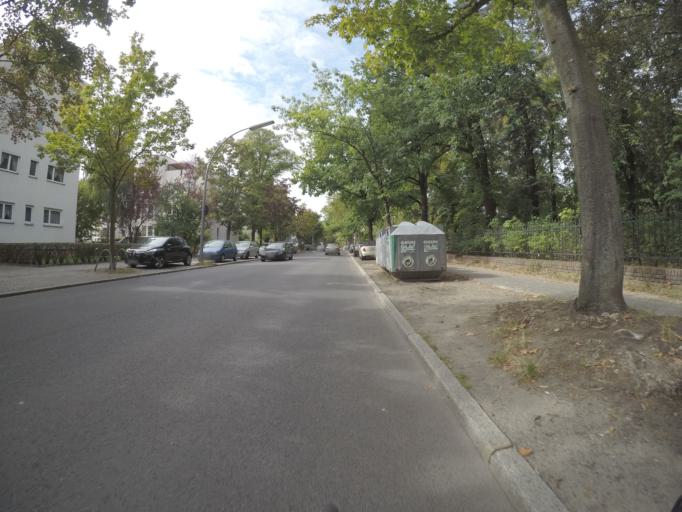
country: DE
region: Berlin
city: Mariendorf
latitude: 52.4475
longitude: 13.3941
